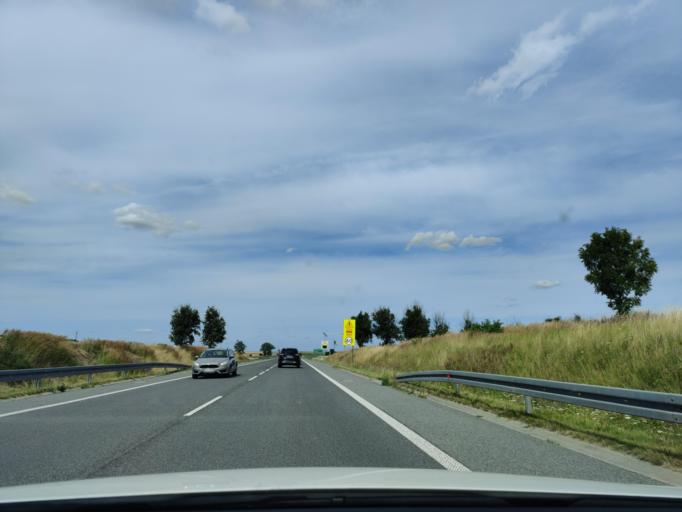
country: PL
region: Opole Voivodeship
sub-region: Powiat prudnicki
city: Biala
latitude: 50.3795
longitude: 17.6733
